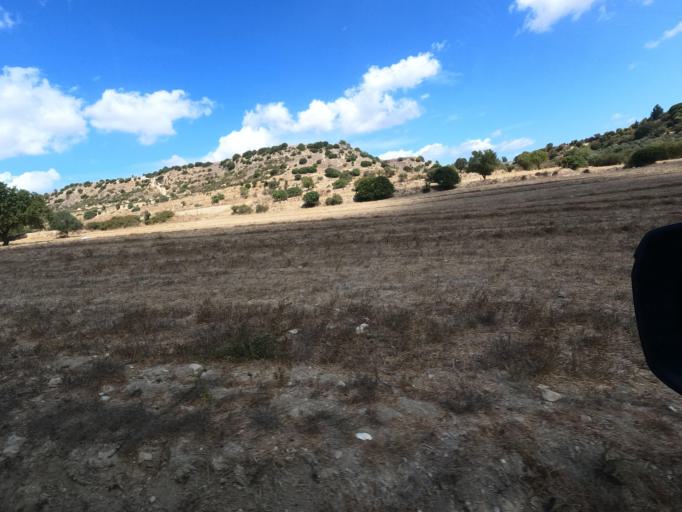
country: CY
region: Pafos
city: Mesogi
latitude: 34.8262
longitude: 32.5506
